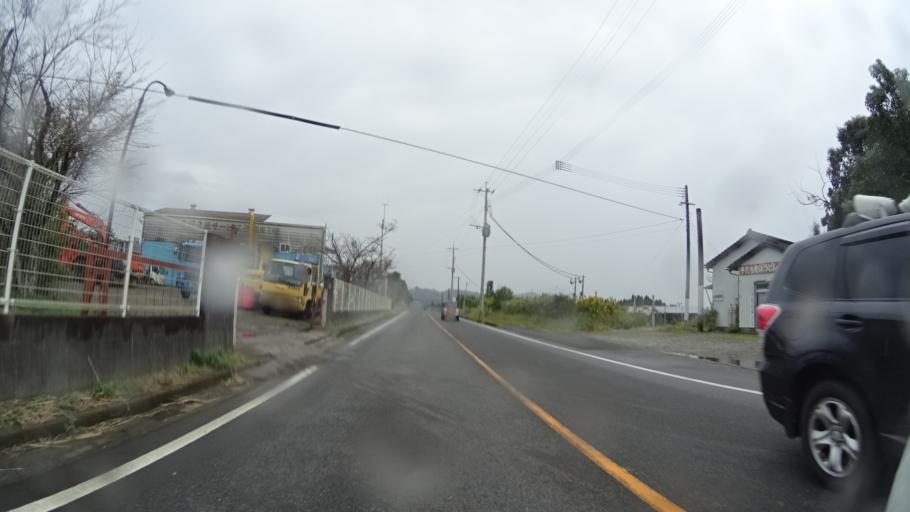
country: JP
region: Kagoshima
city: Kajiki
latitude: 31.8066
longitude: 130.6774
